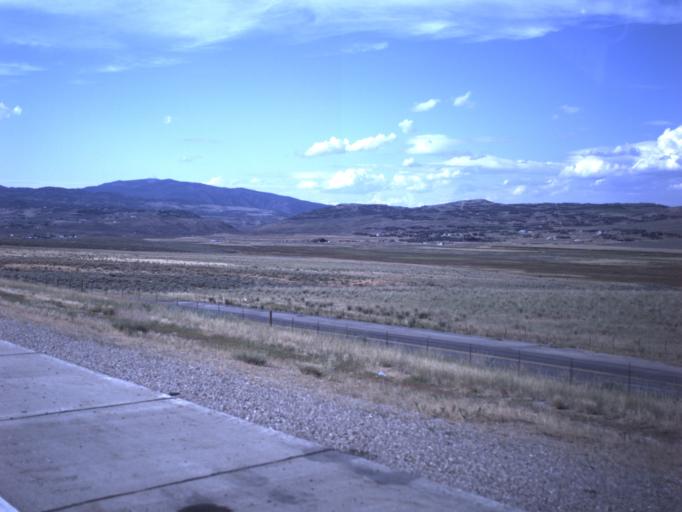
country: US
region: Utah
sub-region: Summit County
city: Park City
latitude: 40.7024
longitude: -111.4750
